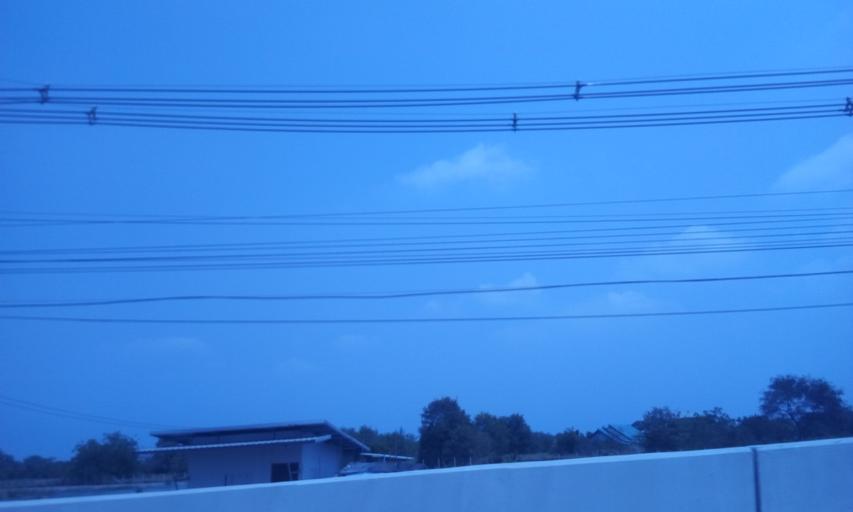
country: TH
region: Chachoengsao
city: Chachoengsao
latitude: 13.7472
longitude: 101.0787
